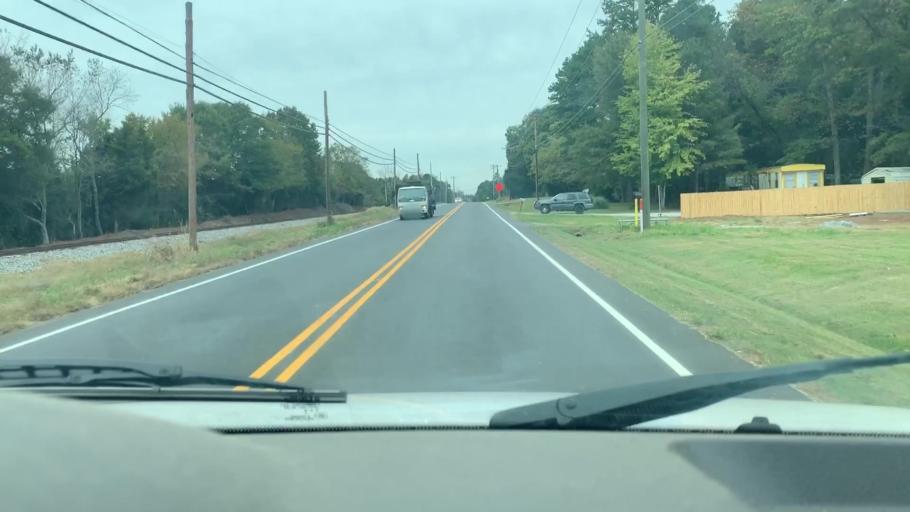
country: US
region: North Carolina
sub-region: Gaston County
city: Davidson
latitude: 35.5220
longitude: -80.8419
